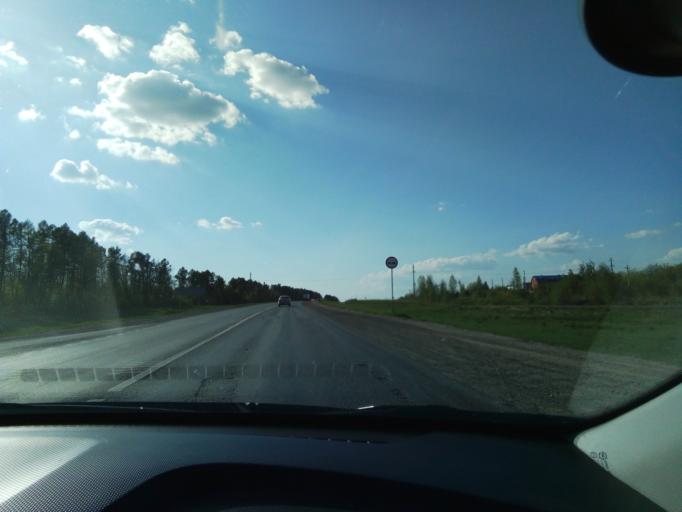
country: RU
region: Chuvashia
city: Novyye Lapsary
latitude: 56.0629
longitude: 47.2454
